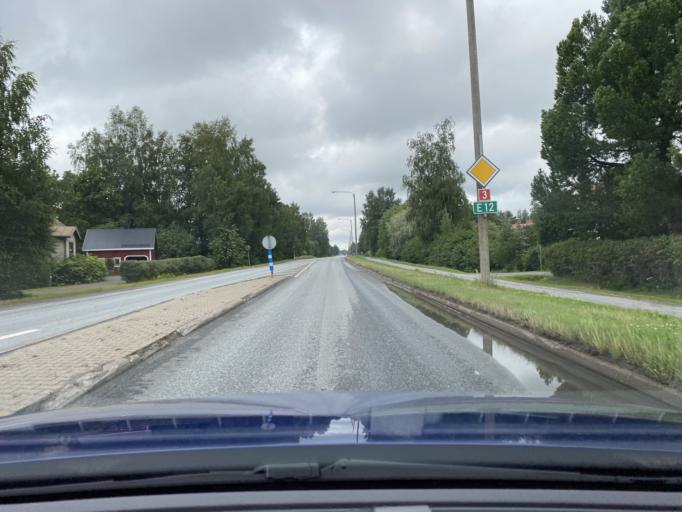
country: FI
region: Ostrobothnia
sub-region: Kyroenmaa
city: Laihia
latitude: 62.9725
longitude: 22.0251
